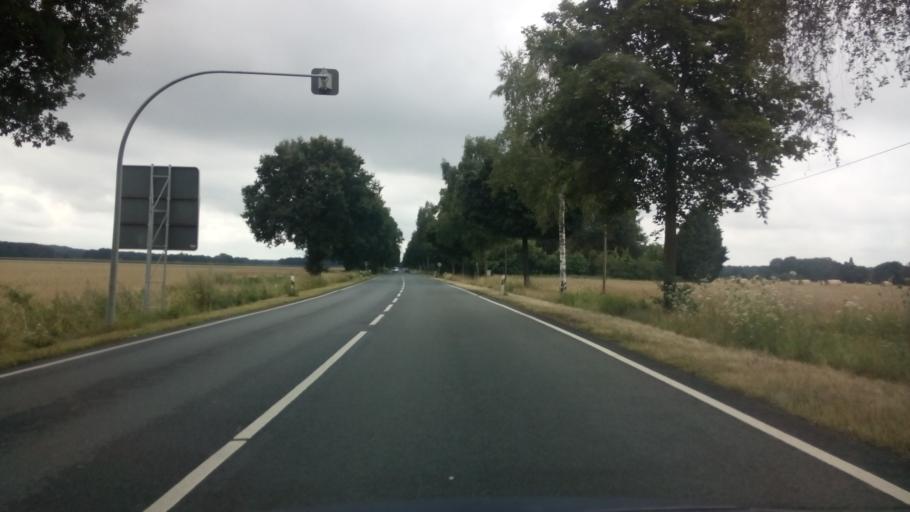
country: DE
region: Lower Saxony
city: Kirchseelte
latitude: 52.9682
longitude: 8.7246
